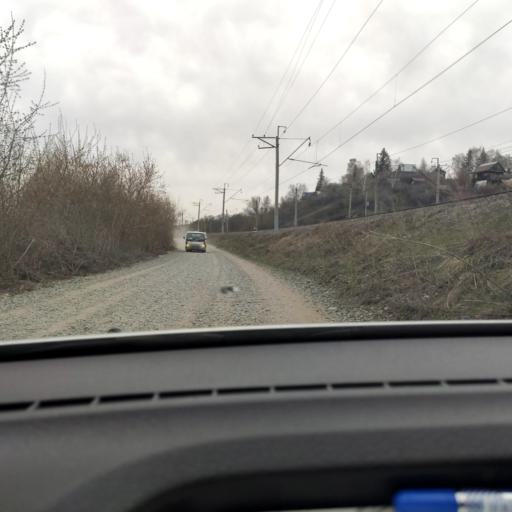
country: RU
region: Bashkortostan
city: Avdon
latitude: 54.6199
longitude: 55.6032
